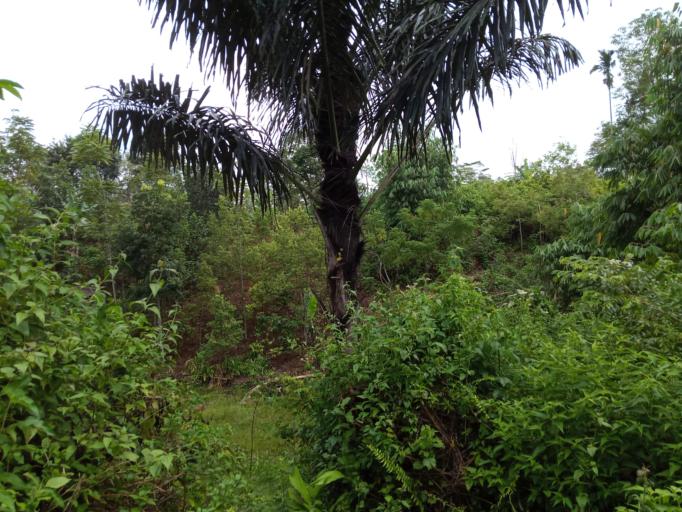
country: ID
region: Jambi
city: Semurup
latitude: -1.9909
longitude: 101.3527
